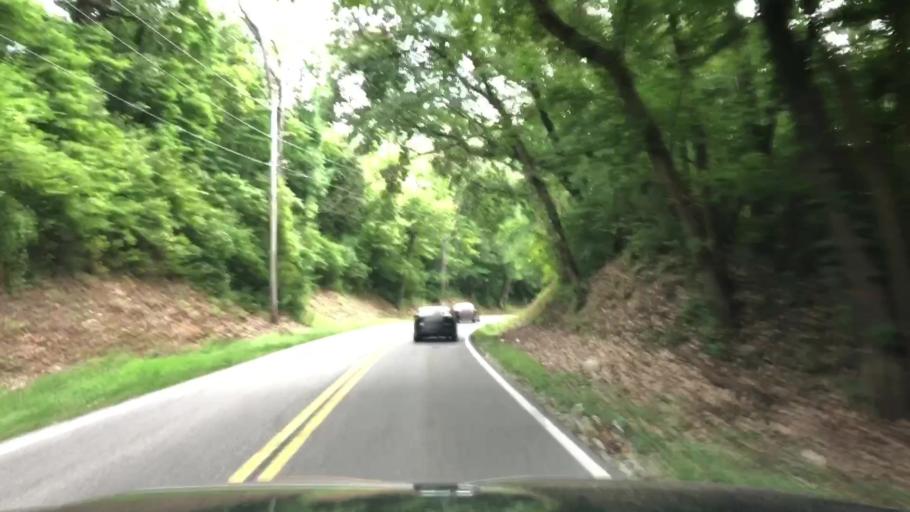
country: US
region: Missouri
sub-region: Saint Louis County
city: Hazelwood
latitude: 38.8108
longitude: -90.3875
